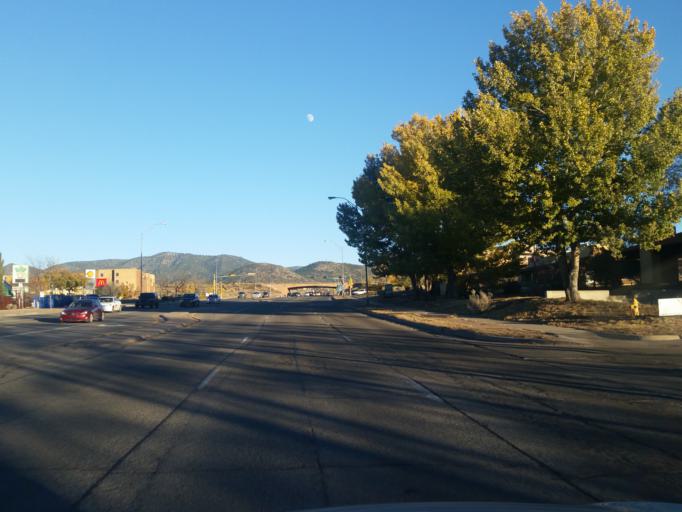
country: US
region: New Mexico
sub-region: Santa Fe County
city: Santa Fe
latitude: 35.6594
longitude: -105.9619
